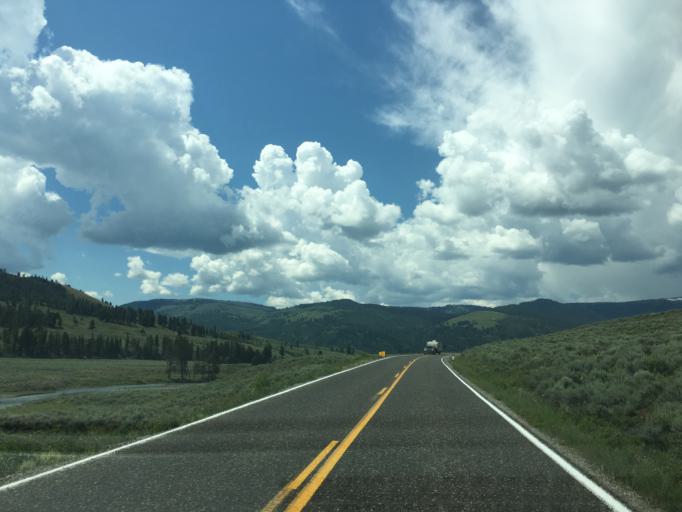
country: US
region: Montana
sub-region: Park County
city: Livingston
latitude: 44.8717
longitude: -110.1635
